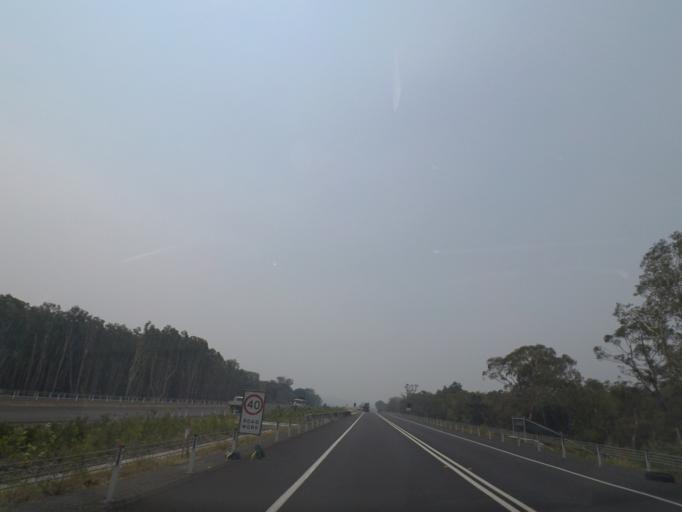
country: AU
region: New South Wales
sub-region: Ballina
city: Ballina
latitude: -28.9117
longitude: 153.4788
